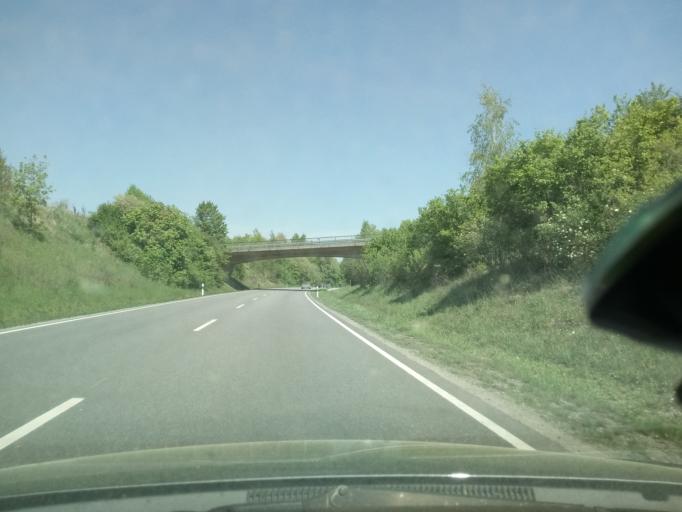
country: DE
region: Bavaria
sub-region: Upper Bavaria
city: Altoetting
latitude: 48.2374
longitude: 12.6543
